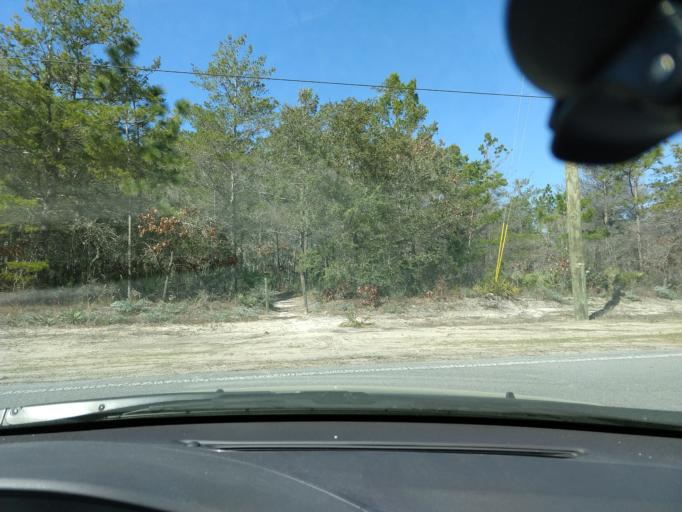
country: US
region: Florida
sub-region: Walton County
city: Seaside
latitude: 30.3473
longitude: -86.1996
